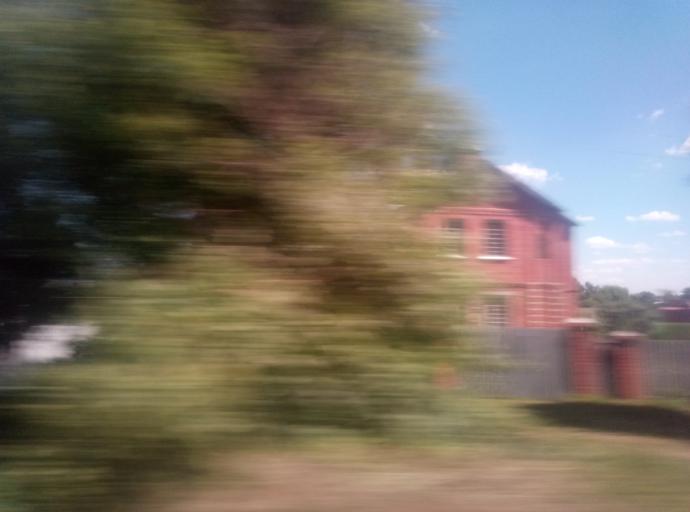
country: RU
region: Tula
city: Kireyevsk
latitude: 53.9685
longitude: 37.9330
